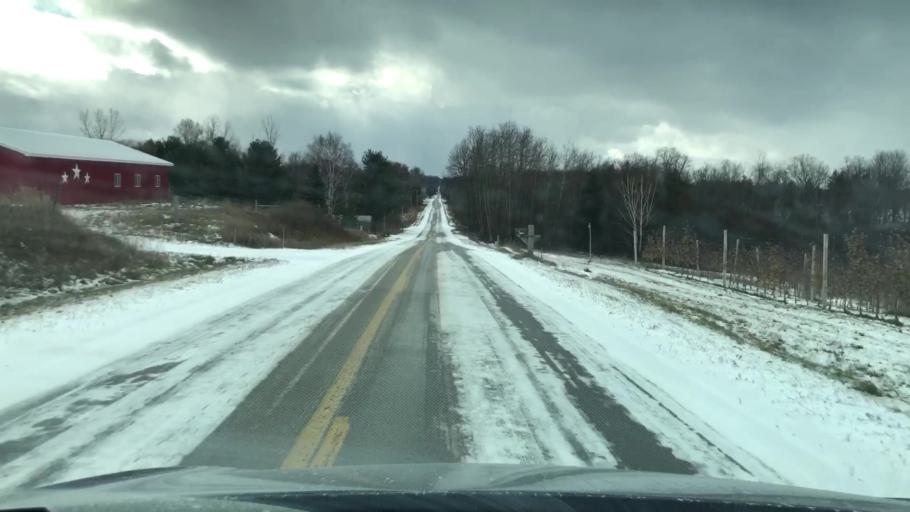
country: US
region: Michigan
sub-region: Antrim County
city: Elk Rapids
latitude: 44.9173
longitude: -85.5155
